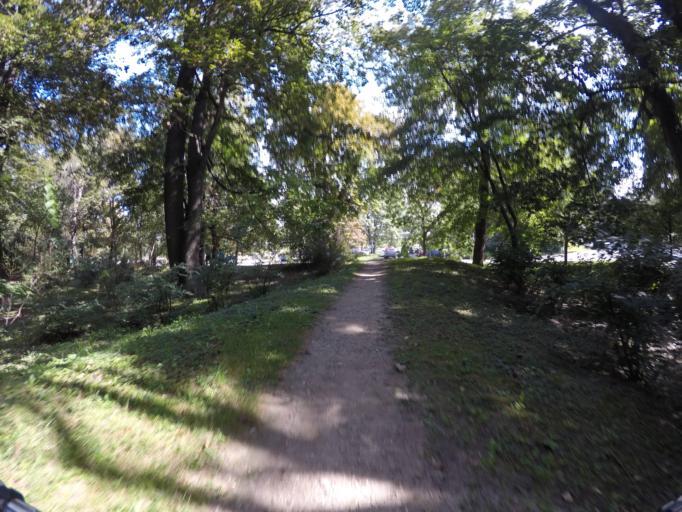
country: SK
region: Bratislavsky
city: Bratislava
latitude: 48.1331
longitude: 17.1140
